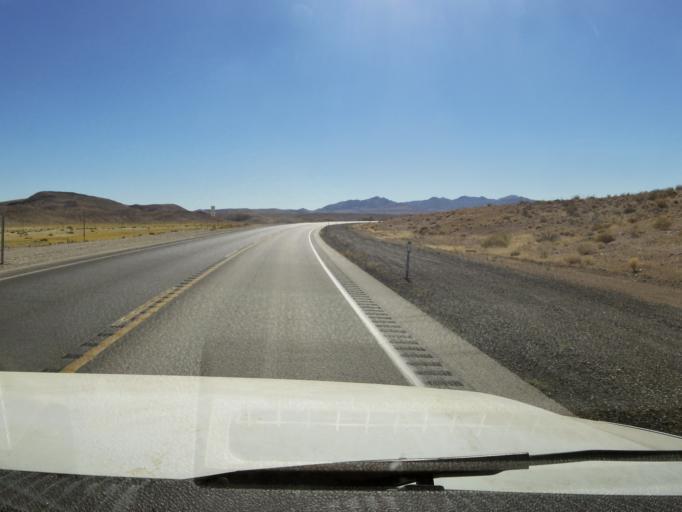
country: US
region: Nevada
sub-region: Nye County
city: Beatty
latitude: 37.0124
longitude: -116.7285
